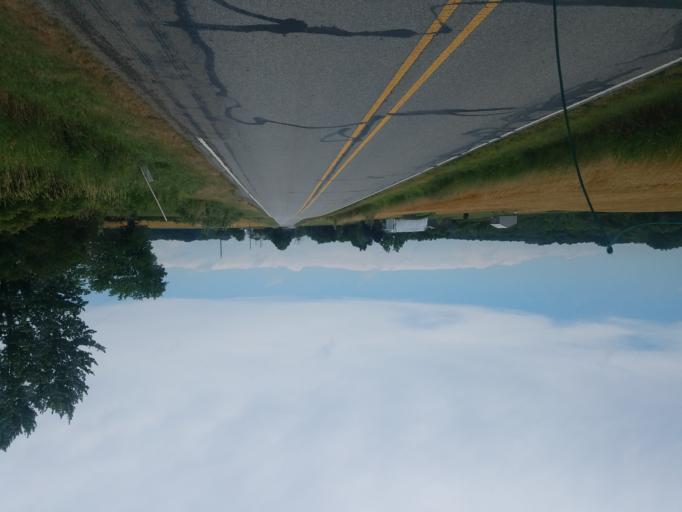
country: US
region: Indiana
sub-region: DeKalb County
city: Butler
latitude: 41.3866
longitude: -84.8282
